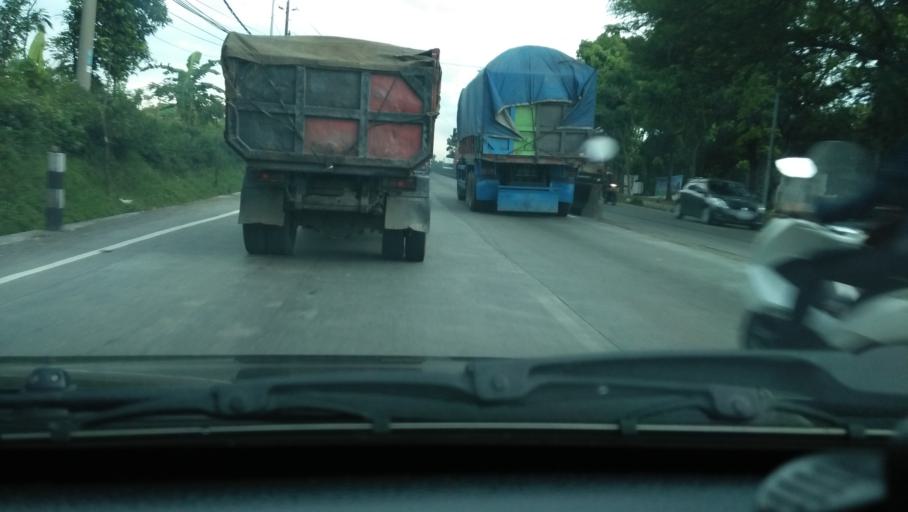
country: ID
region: Central Java
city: Ungaran
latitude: -7.0876
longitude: 110.4087
